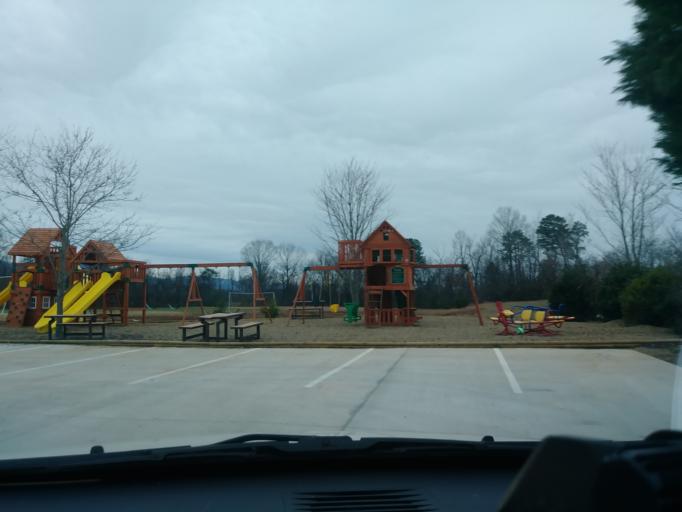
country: US
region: Tennessee
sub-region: Greene County
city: Greeneville
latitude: 36.0682
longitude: -82.8692
